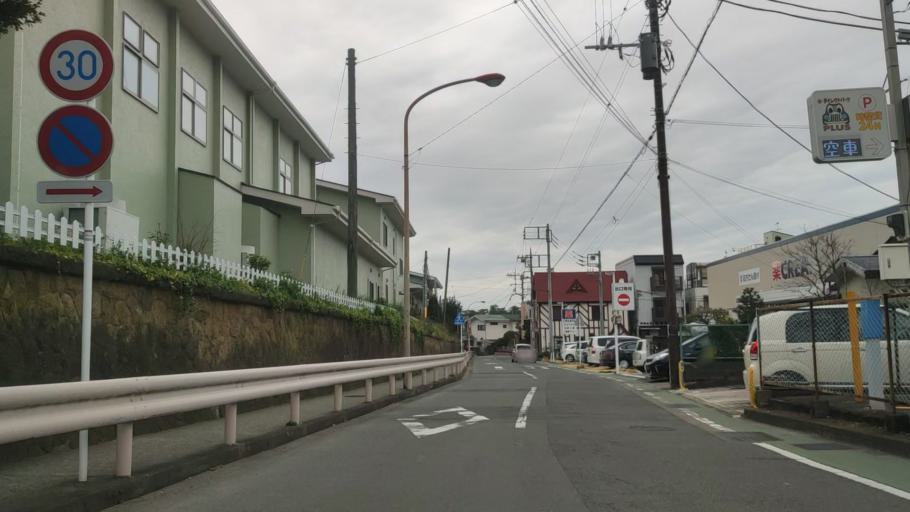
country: JP
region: Kanagawa
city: Oiso
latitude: 35.3106
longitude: 139.3132
